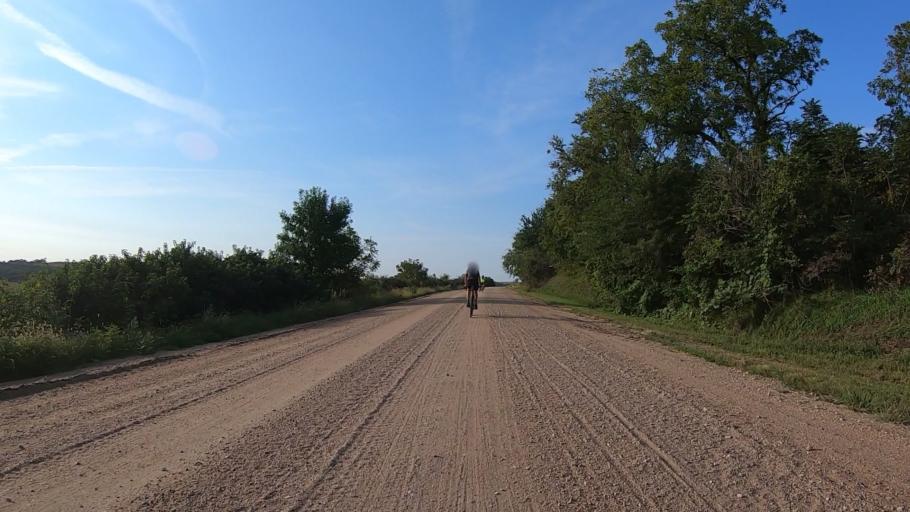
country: US
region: Kansas
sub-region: Marshall County
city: Blue Rapids
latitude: 39.6870
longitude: -96.7790
